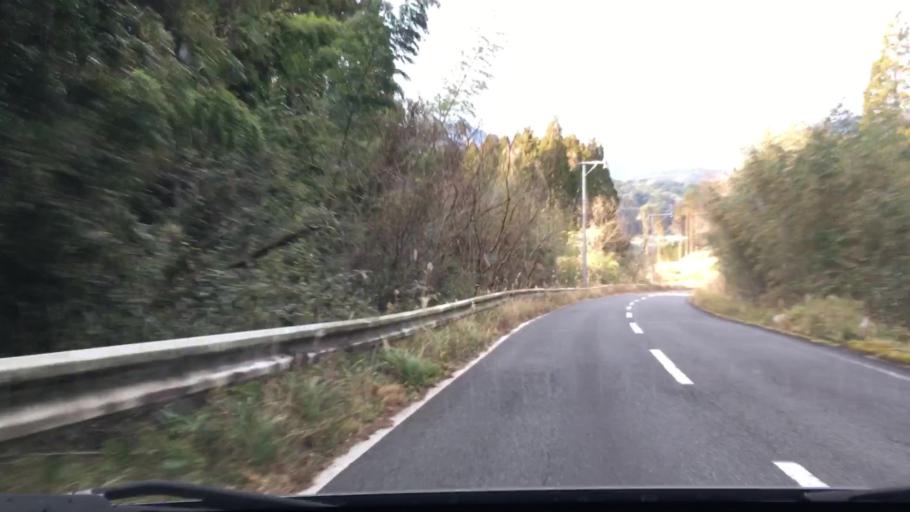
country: JP
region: Miyazaki
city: Nichinan
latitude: 31.6075
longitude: 131.3298
